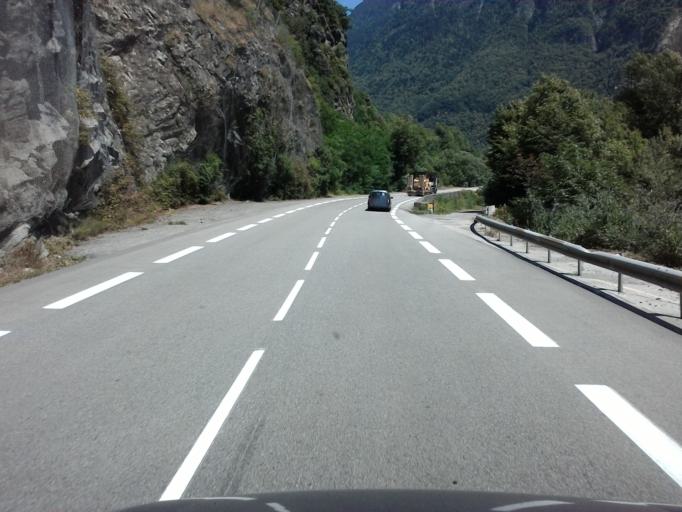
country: FR
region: Rhone-Alpes
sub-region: Departement de l'Isere
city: Vaulnaveys-le-Bas
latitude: 45.0525
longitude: 5.8433
